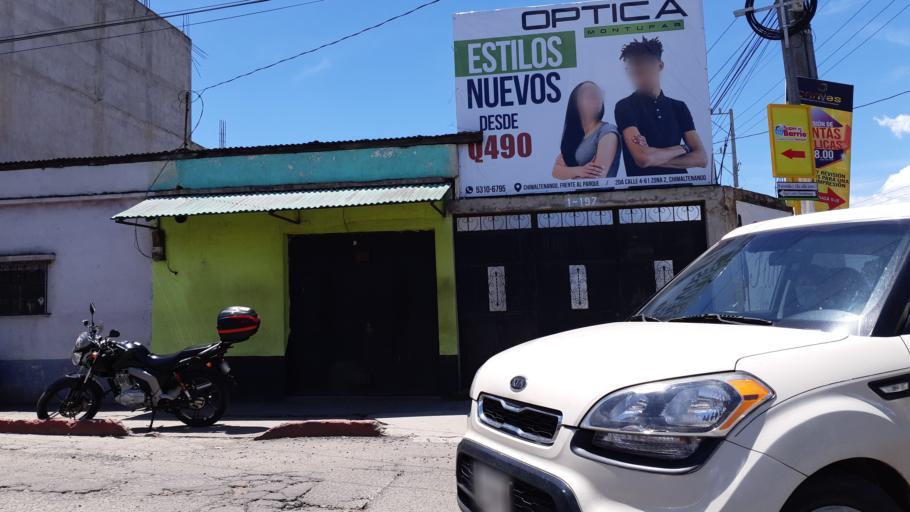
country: GT
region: Chimaltenango
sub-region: Municipio de Chimaltenango
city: Chimaltenango
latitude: 14.6612
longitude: -90.8111
